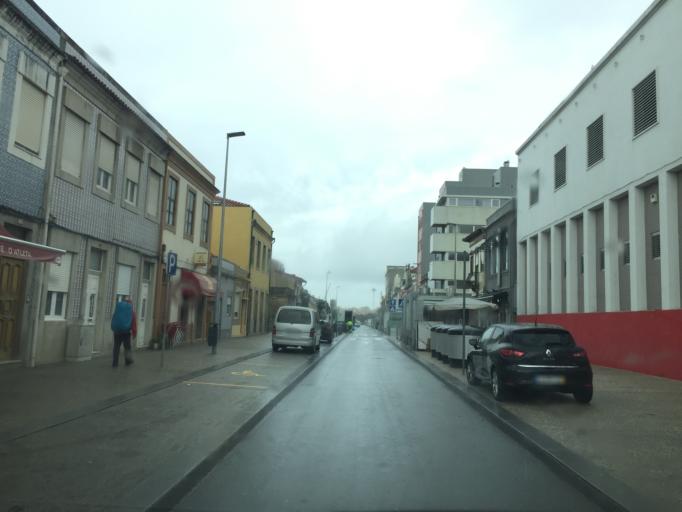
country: PT
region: Porto
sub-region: Matosinhos
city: Matosinhos
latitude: 41.1824
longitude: -8.6942
